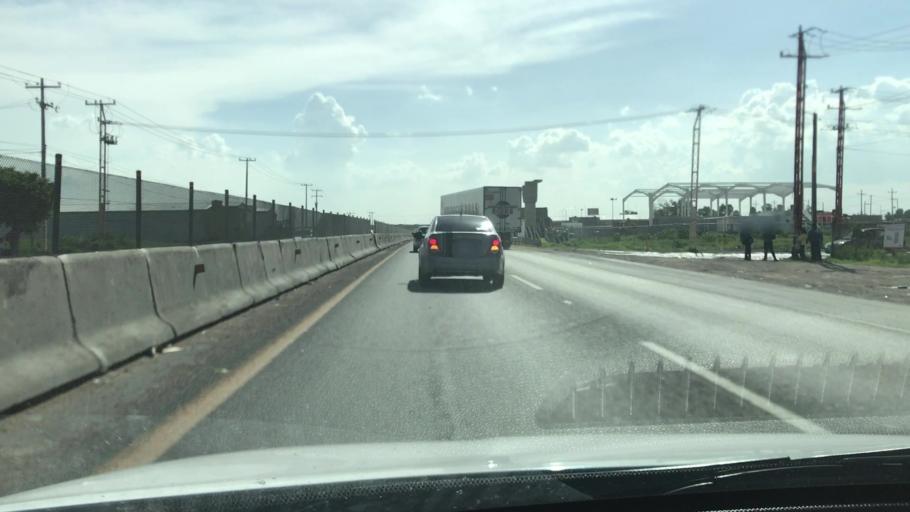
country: MX
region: Guanajuato
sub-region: Celaya
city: Colonia Pedro Maria Anaya
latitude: 20.5176
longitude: -100.8629
